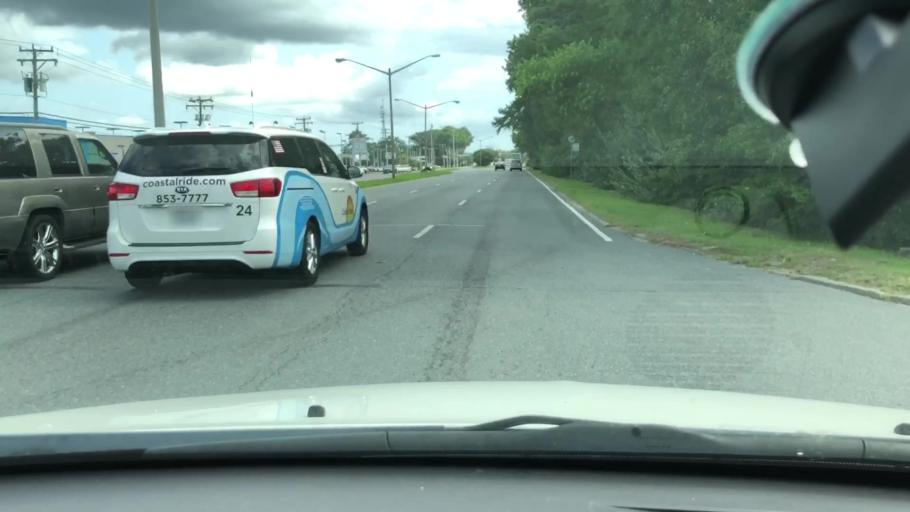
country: US
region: Virginia
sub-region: City of Chesapeake
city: Chesapeake
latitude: 36.7903
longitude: -76.2454
